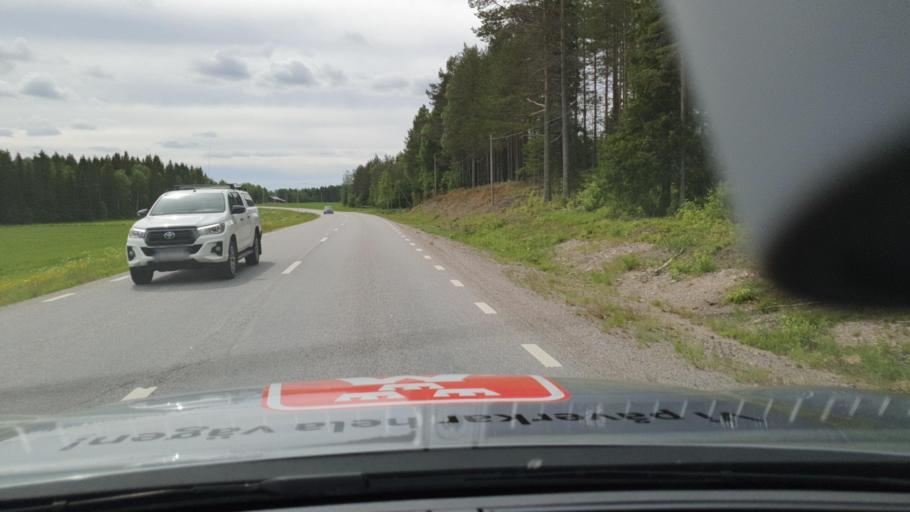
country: SE
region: Norrbotten
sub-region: Kalix Kommun
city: Kalix
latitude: 65.9479
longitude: 23.4551
